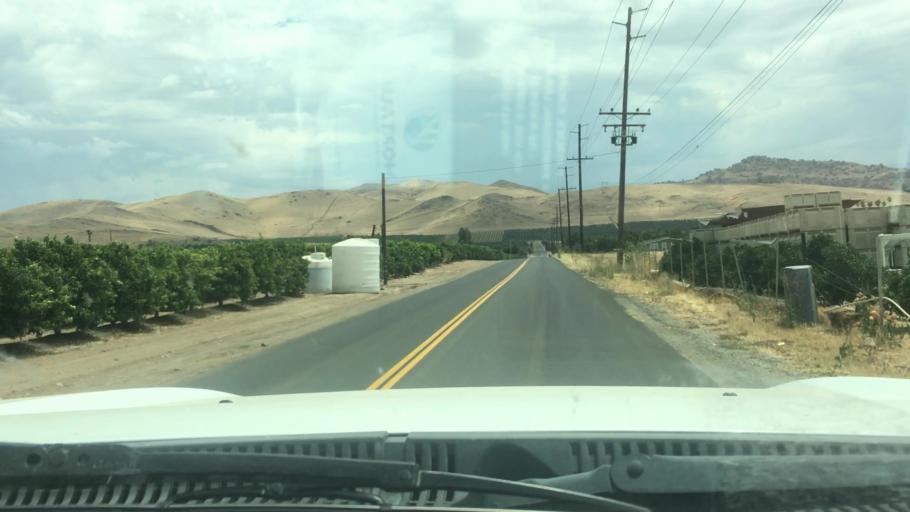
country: US
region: California
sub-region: Tulare County
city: Porterville
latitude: 36.0964
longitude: -119.0252
